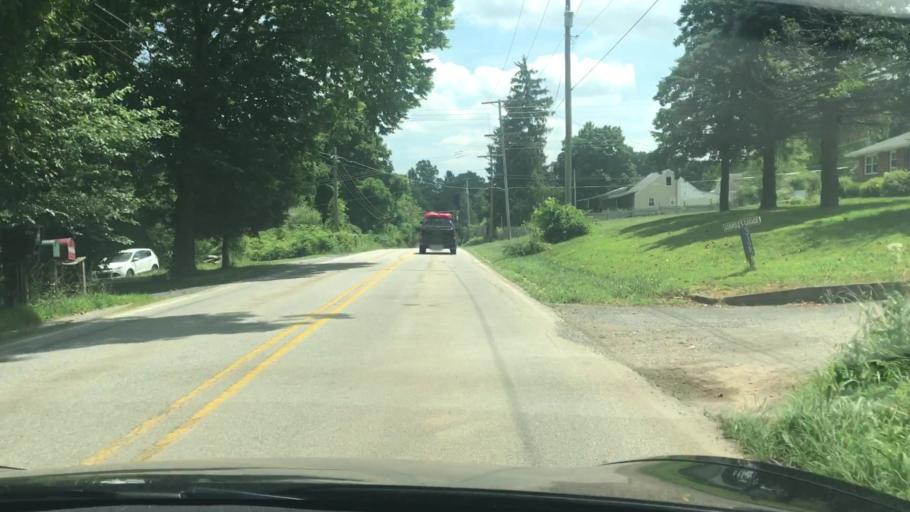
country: US
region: Pennsylvania
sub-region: York County
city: Valley Green
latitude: 40.1152
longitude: -76.7754
